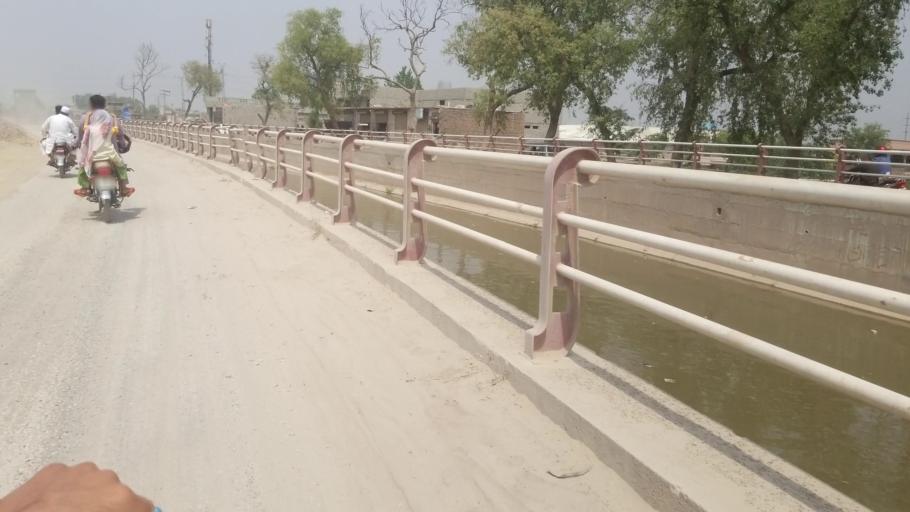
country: PK
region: Khyber Pakhtunkhwa
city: Peshawar
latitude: 33.9670
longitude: 71.5408
